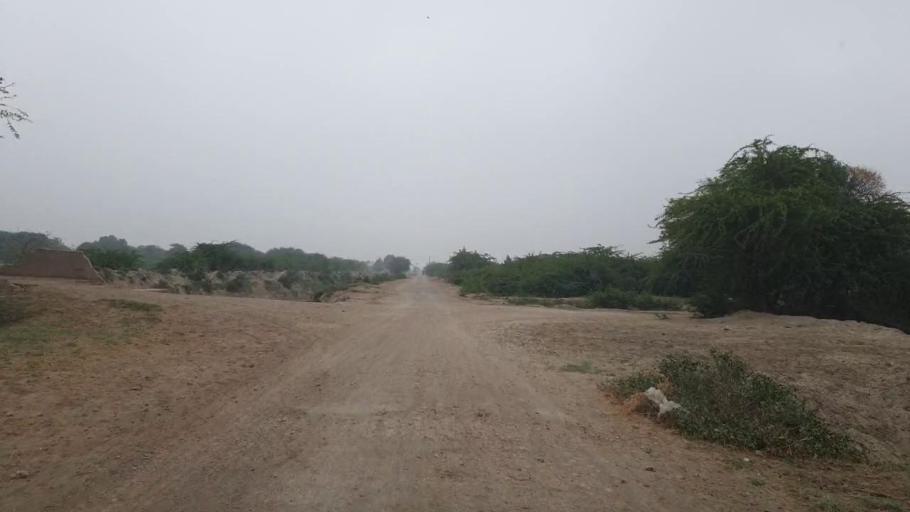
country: PK
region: Sindh
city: Badin
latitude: 24.6063
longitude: 68.6764
